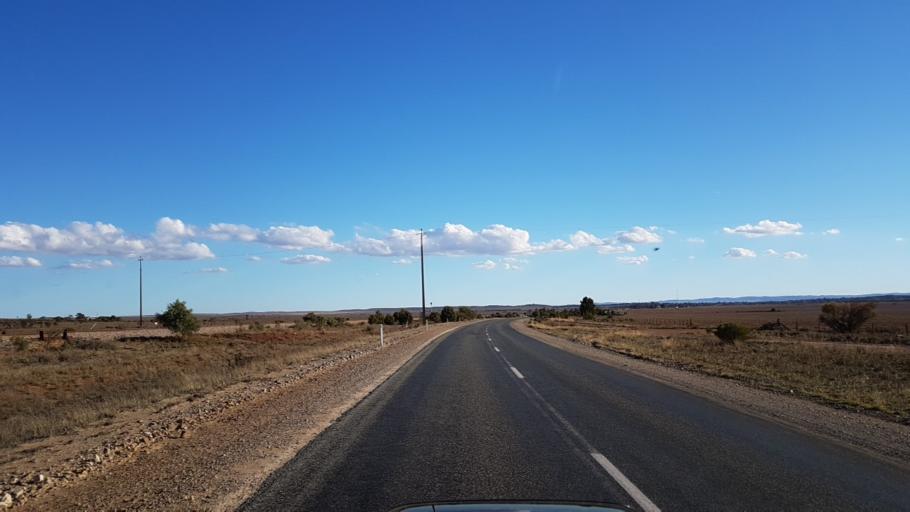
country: AU
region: South Australia
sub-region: Peterborough
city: Peterborough
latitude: -32.9600
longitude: 138.8914
